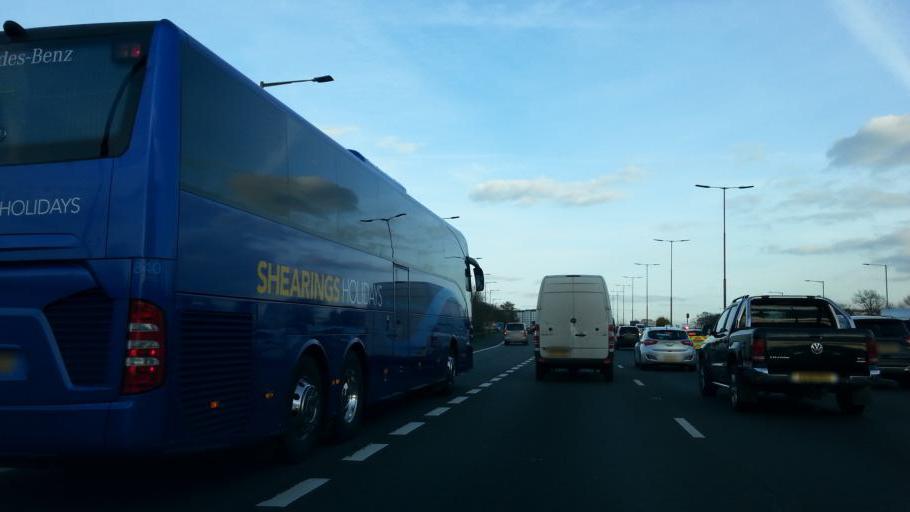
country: GB
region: England
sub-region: Royal Borough of Windsor and Maidenhead
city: Horton
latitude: 51.4899
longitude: -0.5503
